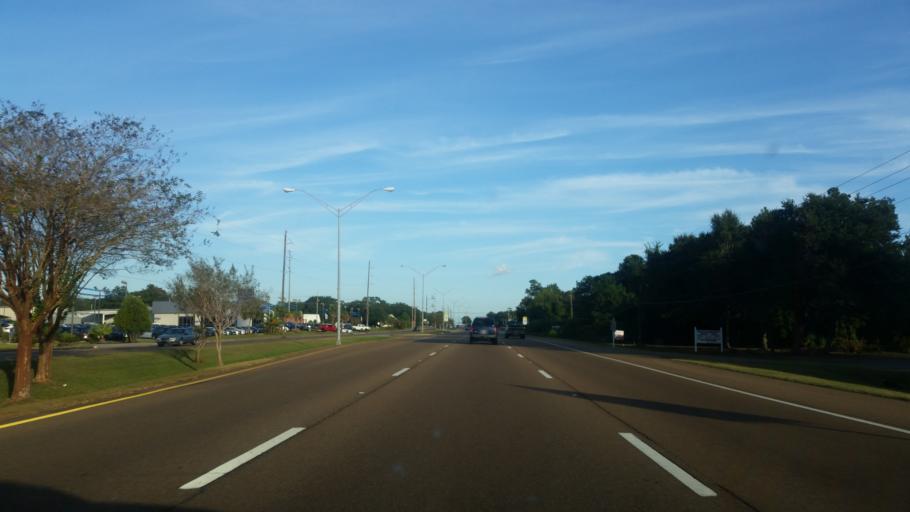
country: US
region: Mississippi
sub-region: Jackson County
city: Gautier
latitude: 30.3858
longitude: -88.6214
